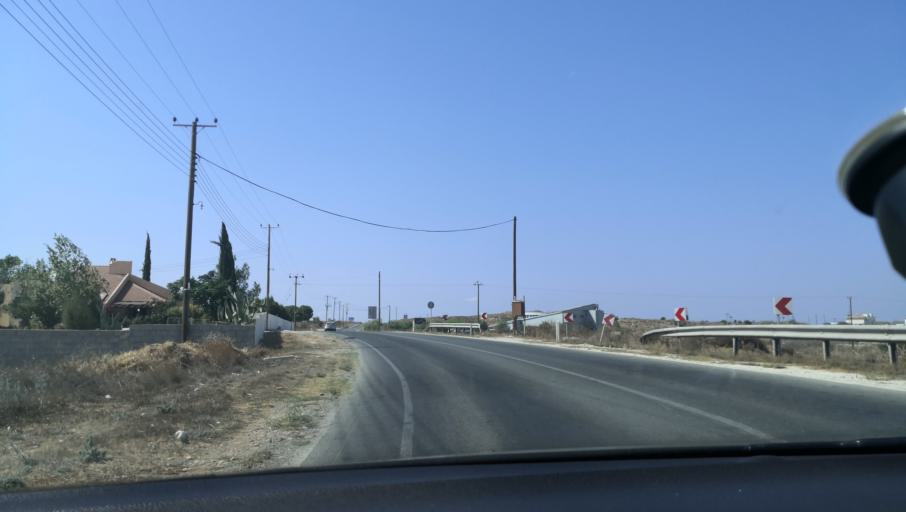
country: CY
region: Lefkosia
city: Kato Deftera
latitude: 35.1210
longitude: 33.2634
